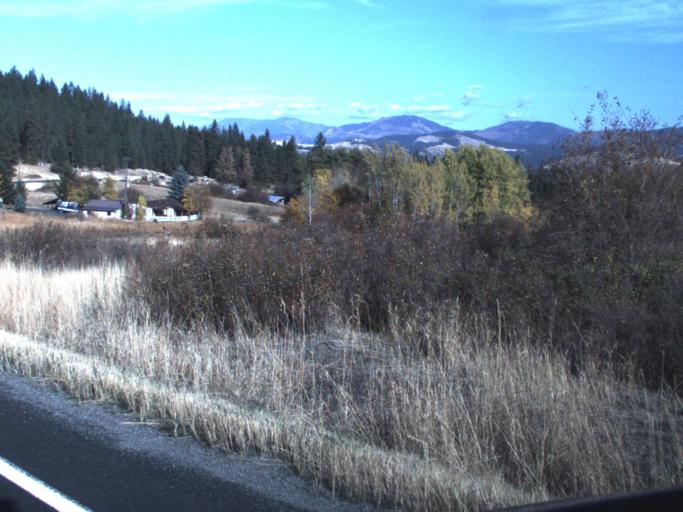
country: US
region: Washington
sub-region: Lincoln County
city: Davenport
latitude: 47.9914
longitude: -118.2873
